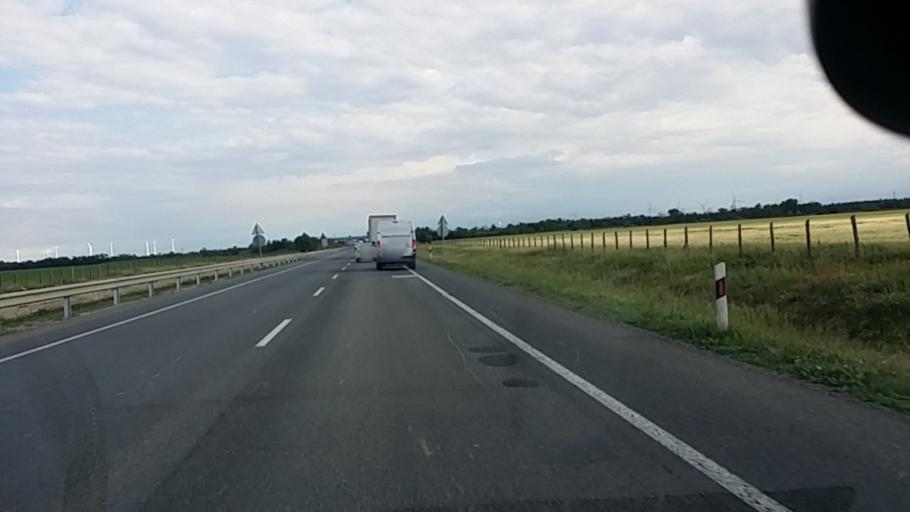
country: HU
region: Gyor-Moson-Sopron
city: Rajka
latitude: 47.9189
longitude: 17.1773
